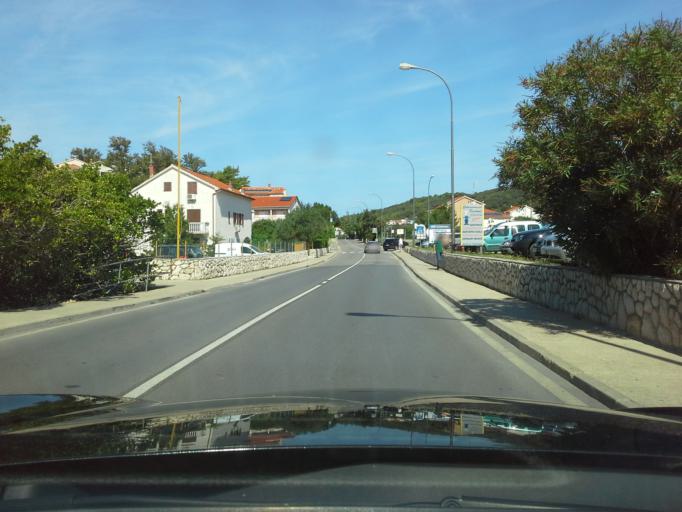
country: HR
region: Primorsko-Goranska
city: Banjol
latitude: 44.7628
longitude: 14.7573
